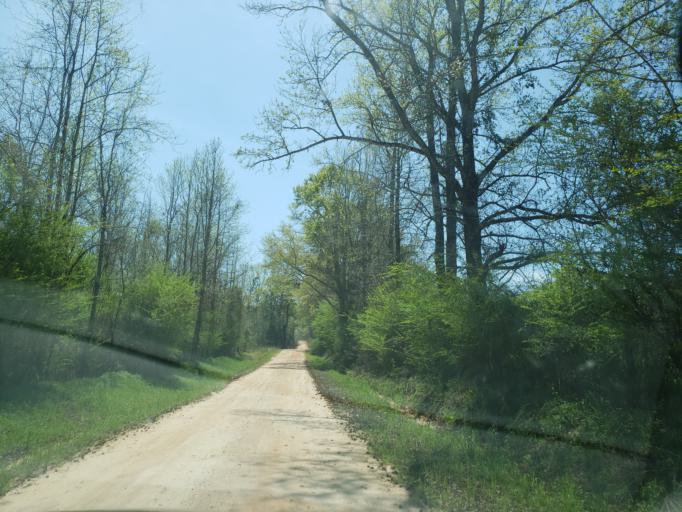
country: US
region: Alabama
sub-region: Tallapoosa County
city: Camp Hill
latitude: 32.6679
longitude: -85.6623
